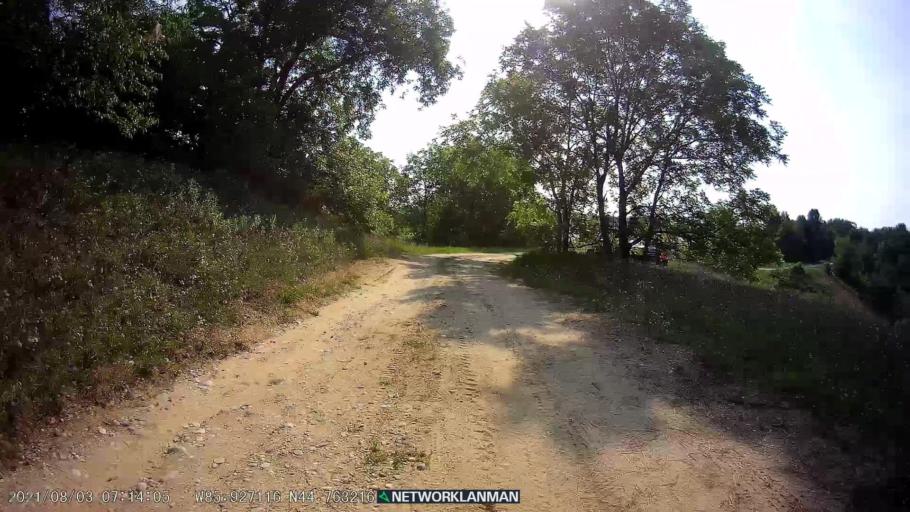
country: US
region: Michigan
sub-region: Benzie County
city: Beulah
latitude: 44.7632
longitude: -85.9273
